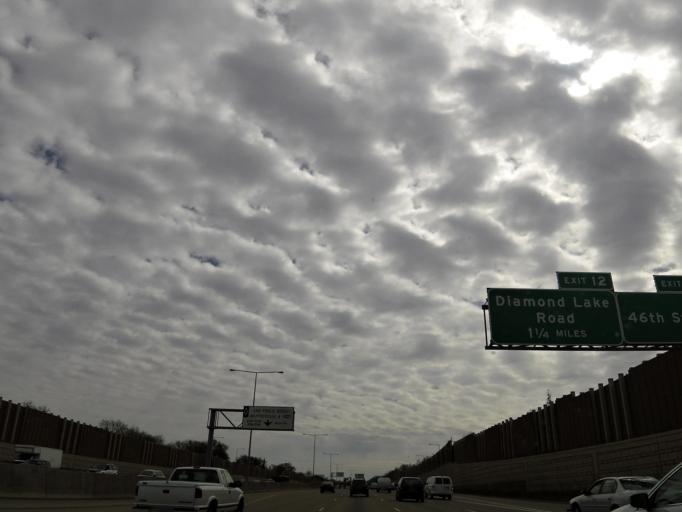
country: US
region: Minnesota
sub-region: Hennepin County
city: Richfield
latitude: 44.9249
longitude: -93.2749
